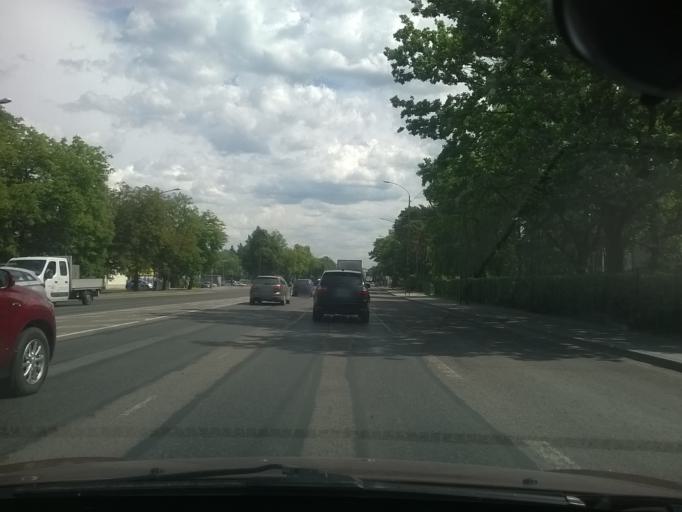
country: EE
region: Harju
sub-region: Tallinna linn
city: Tallinn
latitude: 59.4295
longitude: 24.6951
